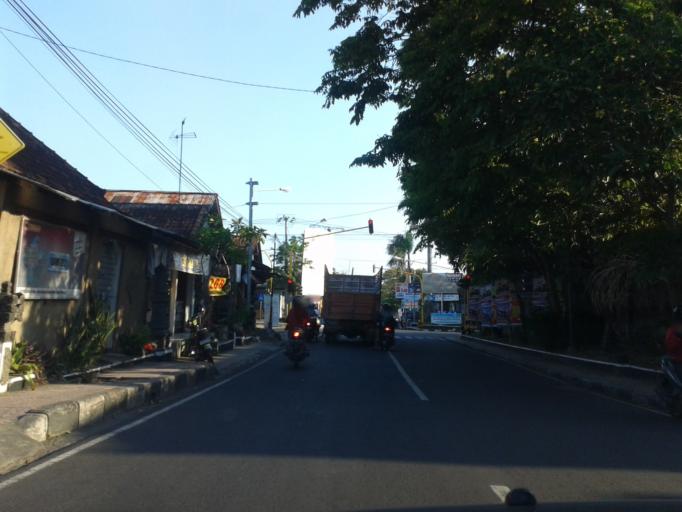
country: ID
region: Bali
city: Semarapura
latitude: -8.5420
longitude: 115.4027
